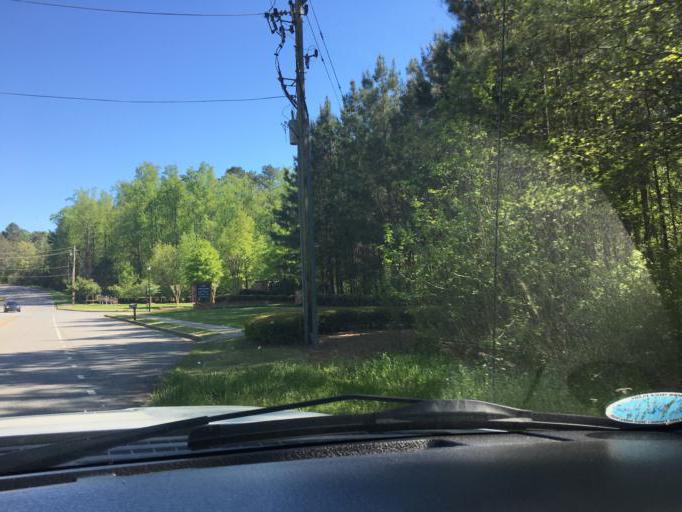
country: US
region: Georgia
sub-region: Forsyth County
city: Cumming
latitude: 34.3089
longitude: -84.1632
